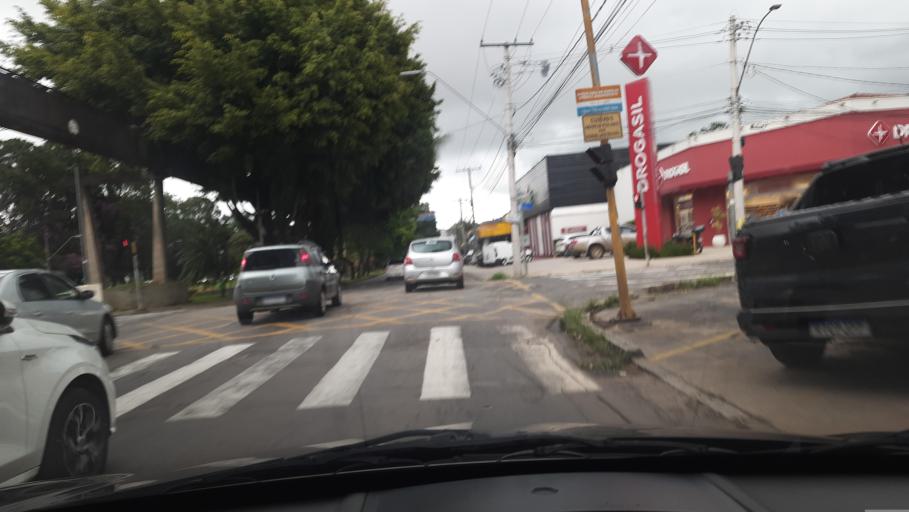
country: BR
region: Minas Gerais
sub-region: Pocos De Caldas
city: Pocos de Caldas
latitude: -21.7850
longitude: -46.5860
